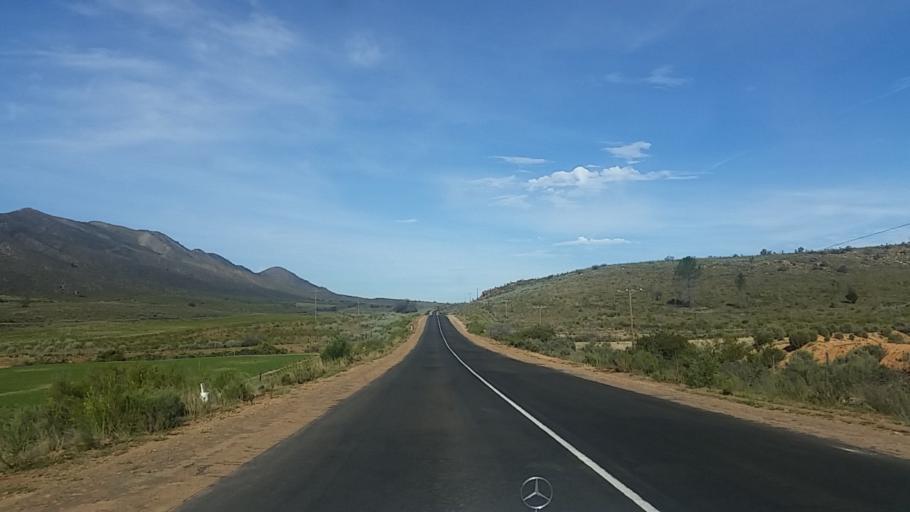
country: ZA
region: Western Cape
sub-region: Eden District Municipality
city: George
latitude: -33.8195
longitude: 22.3639
